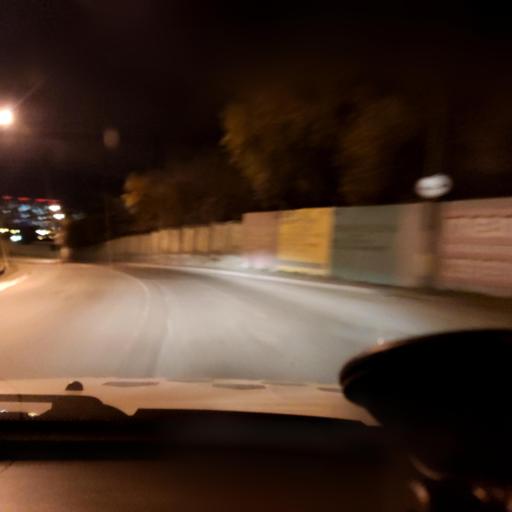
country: RU
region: Perm
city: Perm
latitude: 57.9808
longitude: 56.2712
